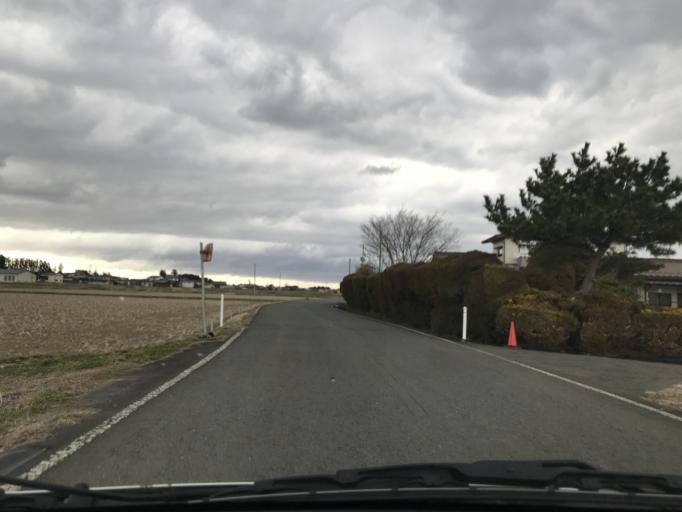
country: JP
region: Iwate
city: Mizusawa
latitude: 39.1009
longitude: 141.1623
